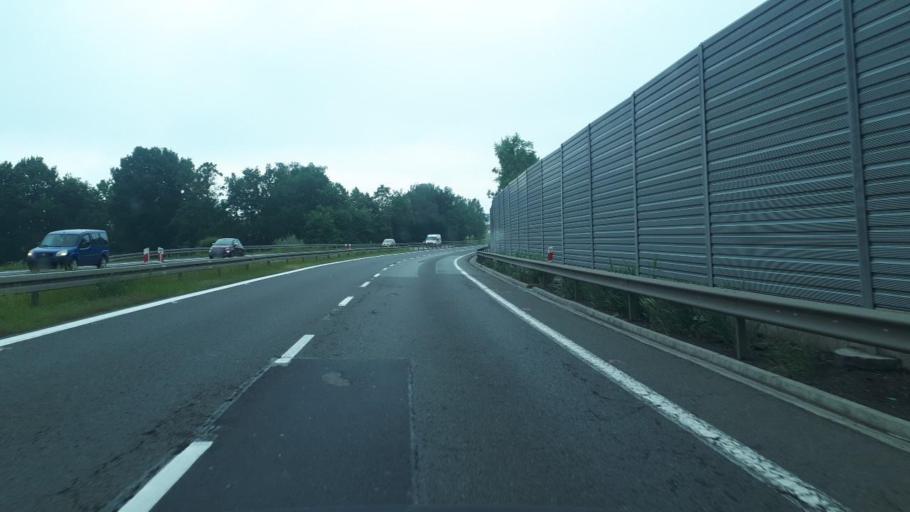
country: PL
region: Silesian Voivodeship
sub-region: Powiat bielski
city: Mazancowice
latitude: 49.8772
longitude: 18.9986
